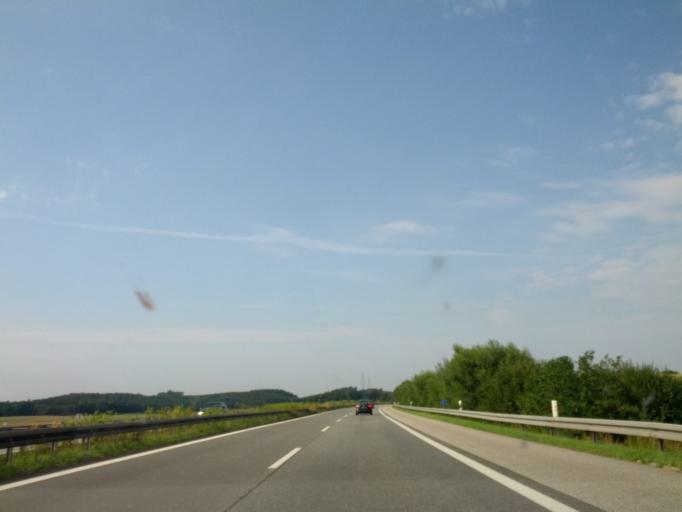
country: DE
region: Mecklenburg-Vorpommern
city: Lalendorf
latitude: 53.7098
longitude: 12.3574
